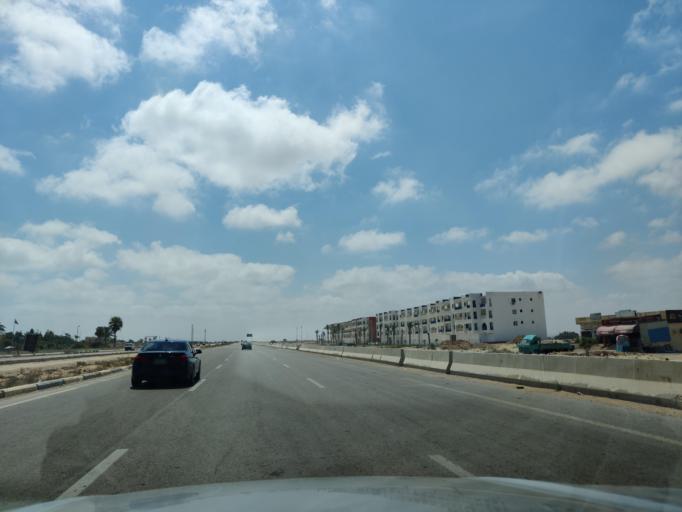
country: EG
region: Muhafazat Matruh
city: Al `Alamayn
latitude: 30.8175
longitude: 29.0287
